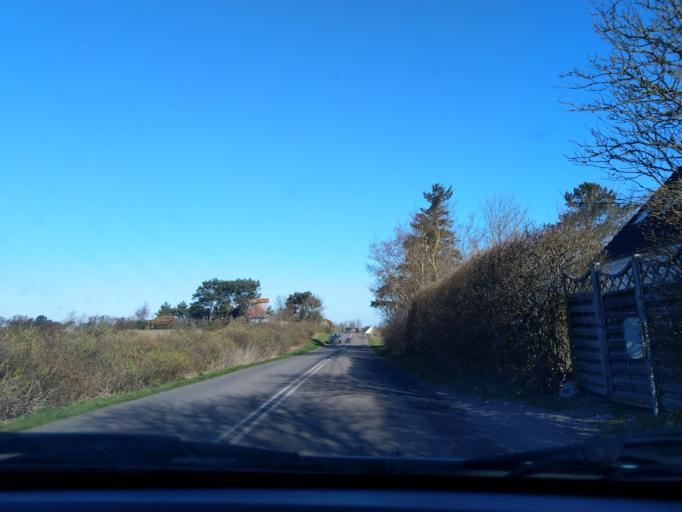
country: DK
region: Zealand
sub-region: Kalundborg Kommune
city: Kalundborg
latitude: 55.7180
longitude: 11.0126
